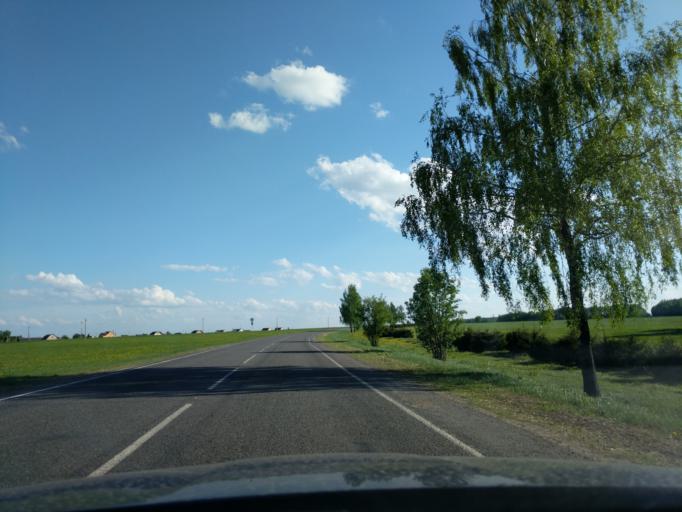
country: BY
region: Minsk
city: Kryvichy
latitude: 54.6932
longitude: 27.1557
